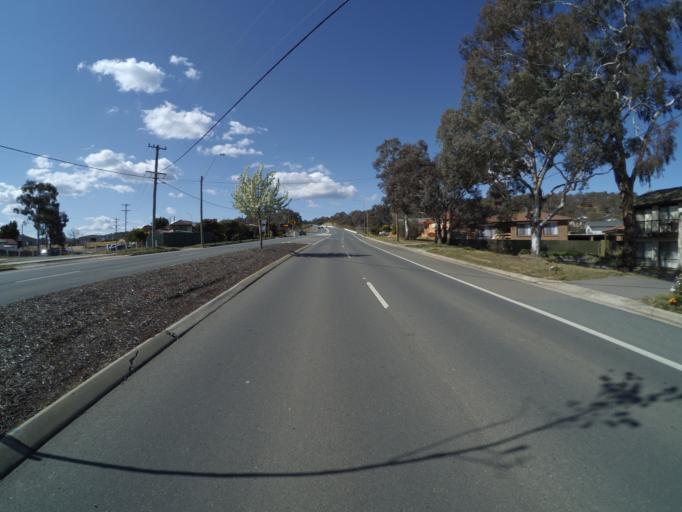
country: AU
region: New South Wales
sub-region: Queanbeyan
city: Queanbeyan
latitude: -35.3456
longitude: 149.2486
